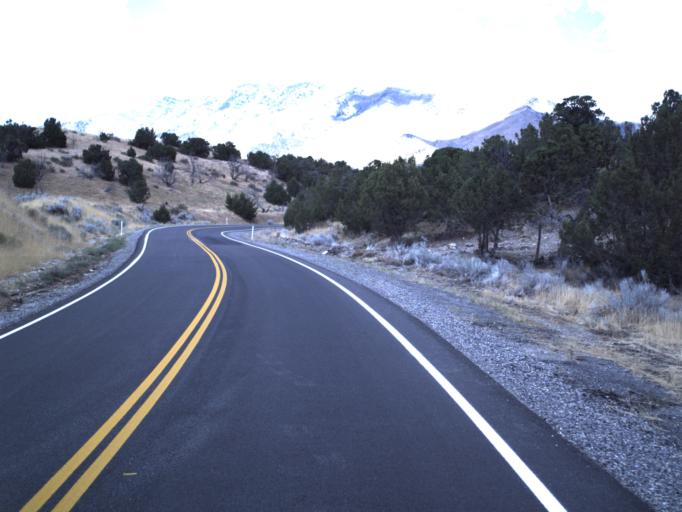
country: US
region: Utah
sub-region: Tooele County
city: Grantsville
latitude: 40.3249
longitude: -112.6242
